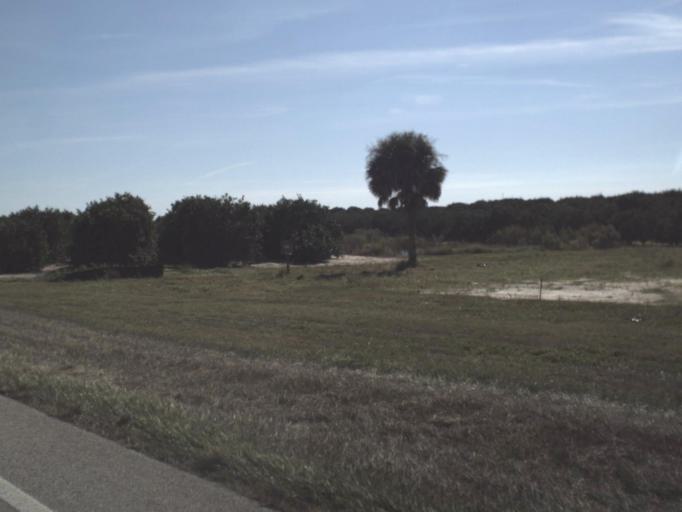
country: US
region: Florida
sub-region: Highlands County
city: Lake Placid
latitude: 27.2341
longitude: -81.3302
